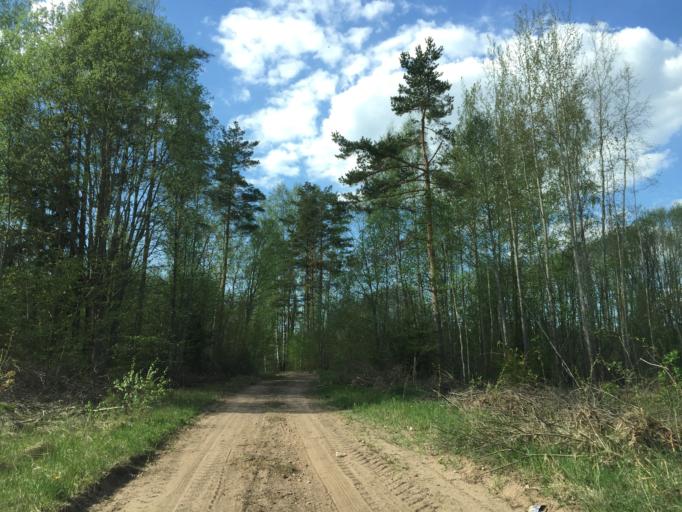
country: LV
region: Limbazu Rajons
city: Limbazi
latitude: 57.4183
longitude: 24.6880
